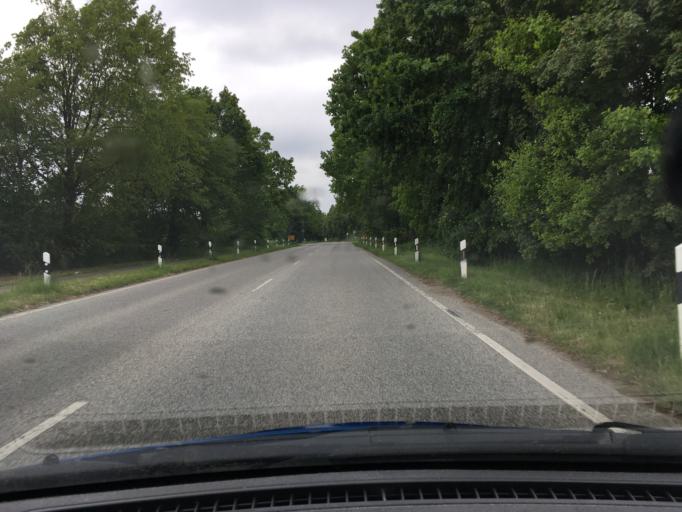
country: DE
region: Schleswig-Holstein
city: Gross Gronau
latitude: 53.7948
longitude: 10.7563
